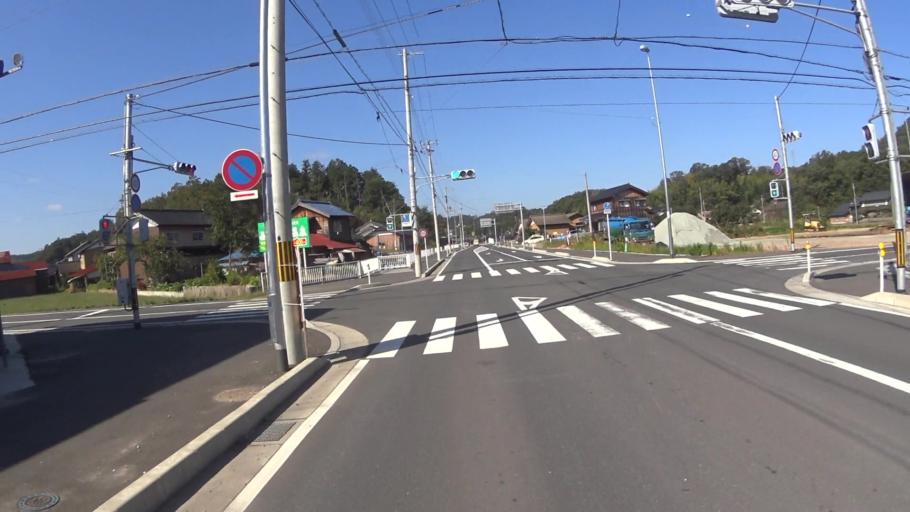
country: JP
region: Kyoto
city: Miyazu
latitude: 35.6706
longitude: 135.0801
